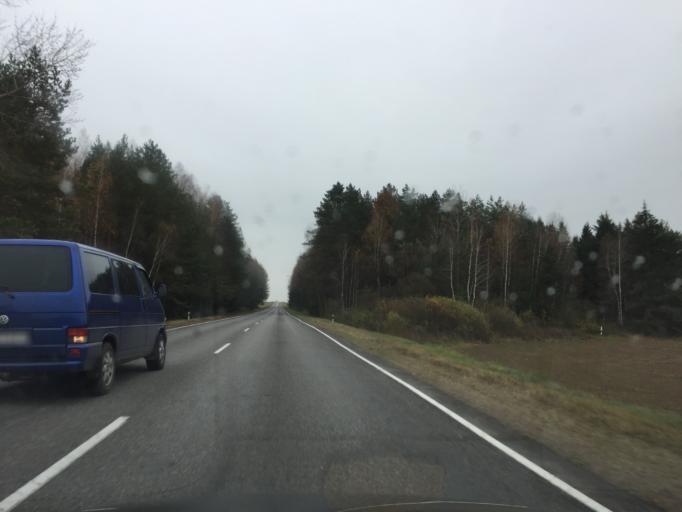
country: BY
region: Mogilev
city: Cherykaw
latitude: 53.6679
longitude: 31.2236
